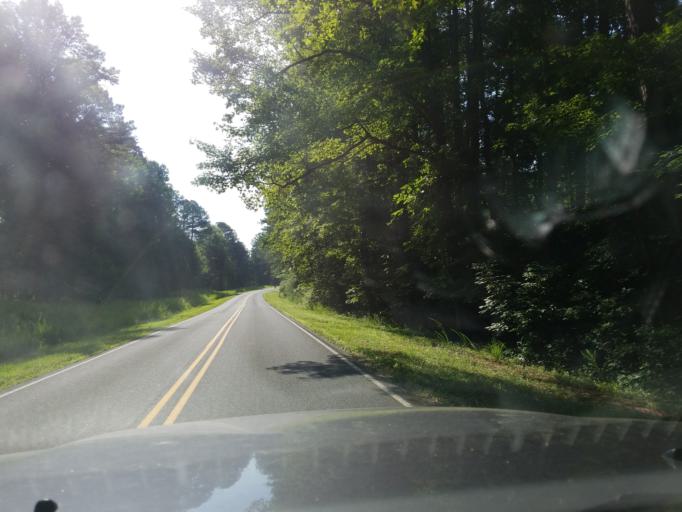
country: US
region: North Carolina
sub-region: Granville County
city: Butner
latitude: 36.1836
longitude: -78.8111
